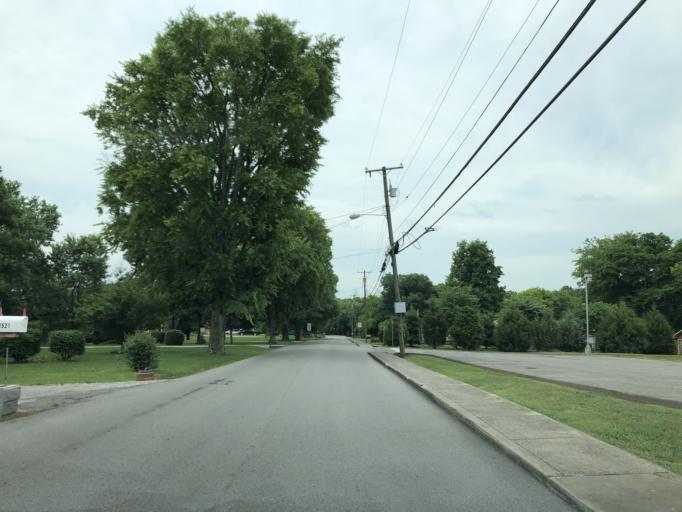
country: US
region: Tennessee
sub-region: Davidson County
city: Goodlettsville
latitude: 36.2914
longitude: -86.7104
